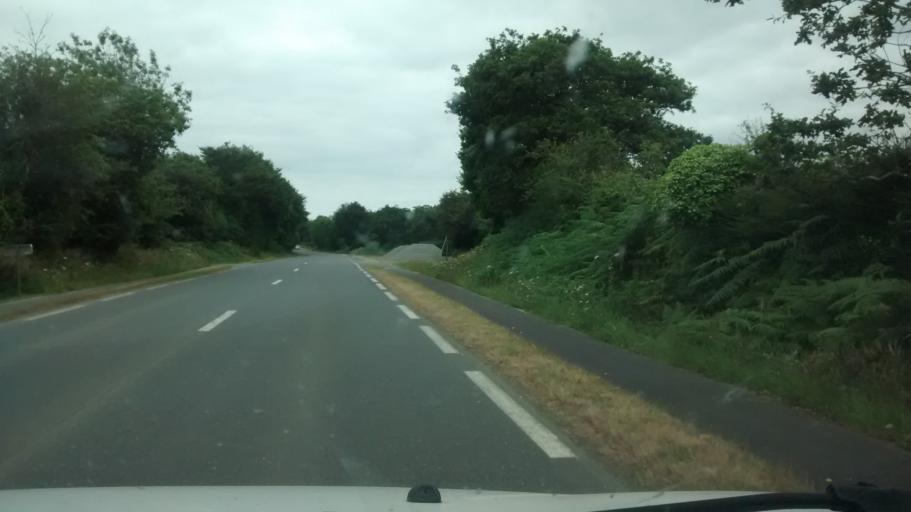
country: FR
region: Brittany
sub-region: Departement du Finistere
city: Plougastel-Daoulas
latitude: 48.3631
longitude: -4.3785
